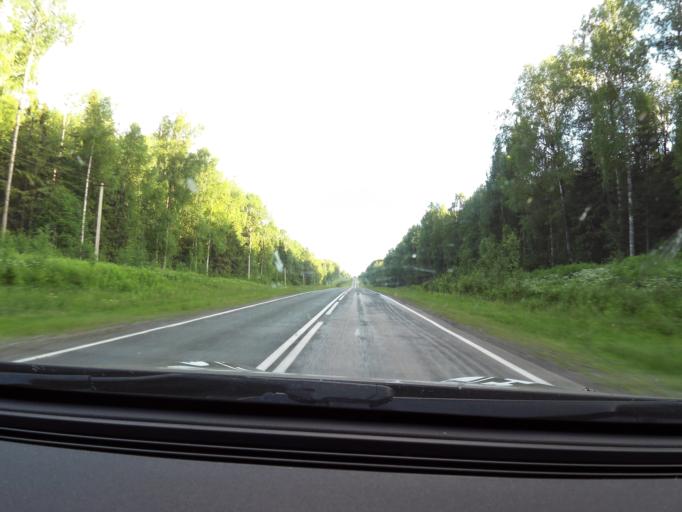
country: RU
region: Perm
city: Siva
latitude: 58.6163
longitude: 53.8710
